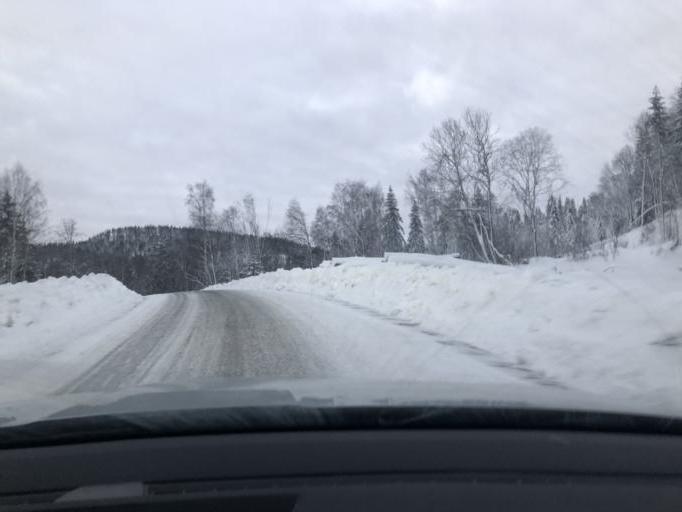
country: SE
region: Vaesternorrland
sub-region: Kramfors Kommun
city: Nordingra
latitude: 62.9174
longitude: 18.2327
